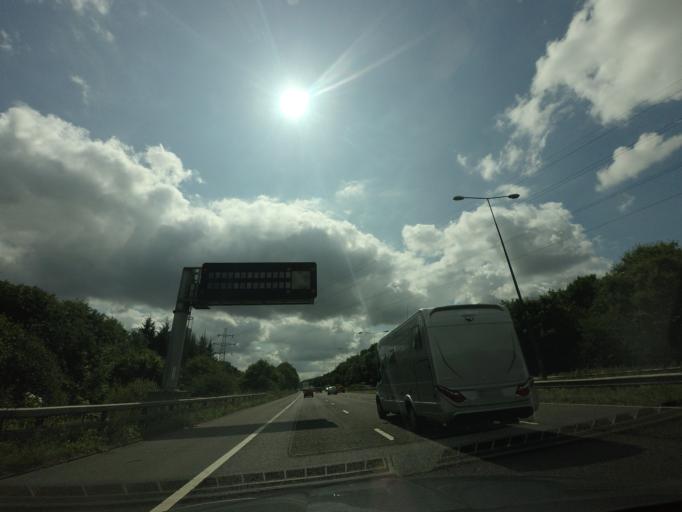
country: GB
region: England
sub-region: St. Helens
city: Billinge
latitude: 53.5266
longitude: -2.6980
